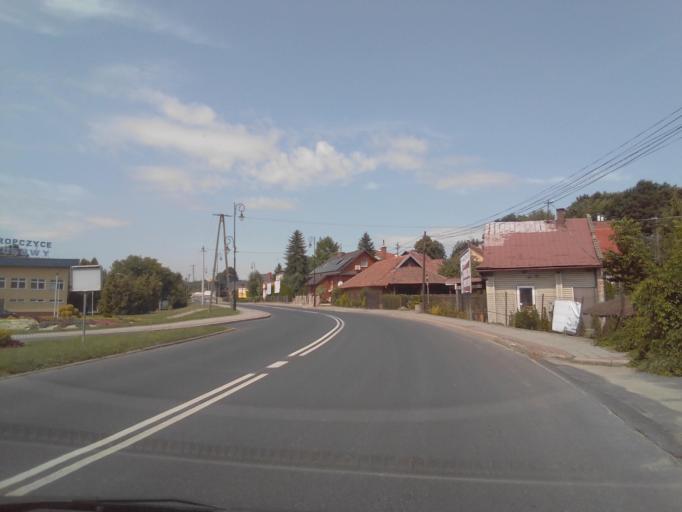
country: PL
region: Subcarpathian Voivodeship
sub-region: Powiat ropczycko-sedziszowski
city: Ropczyce
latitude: 50.0534
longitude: 21.6067
